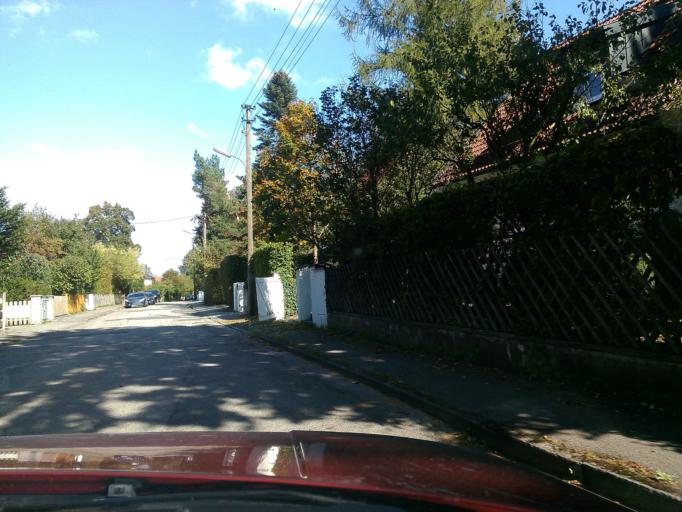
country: DE
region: Bavaria
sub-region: Upper Bavaria
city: Krailling
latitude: 48.0837
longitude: 11.4048
